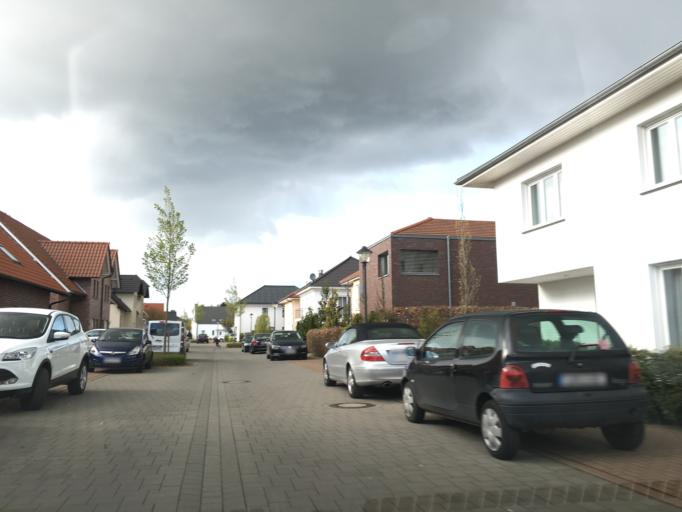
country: DE
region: North Rhine-Westphalia
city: Ludinghausen
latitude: 51.7761
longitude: 7.4534
